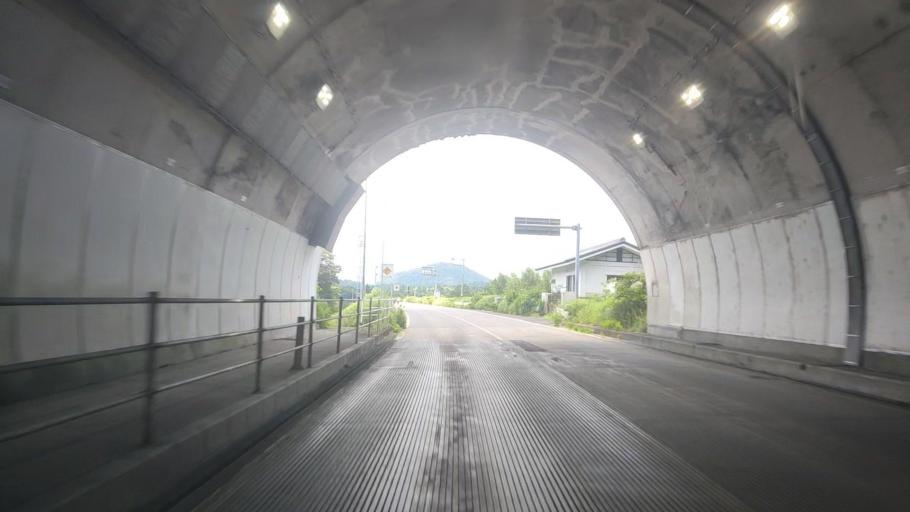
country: JP
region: Gifu
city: Tarui
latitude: 35.3724
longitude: 136.4557
